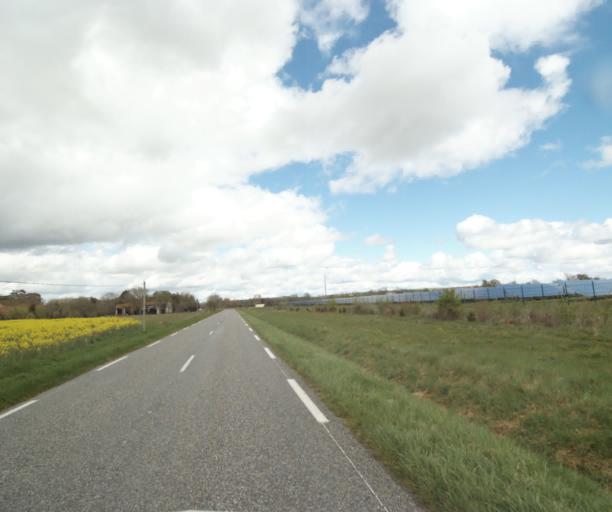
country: FR
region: Midi-Pyrenees
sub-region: Departement de l'Ariege
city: Mazeres
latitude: 43.2390
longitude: 1.6362
